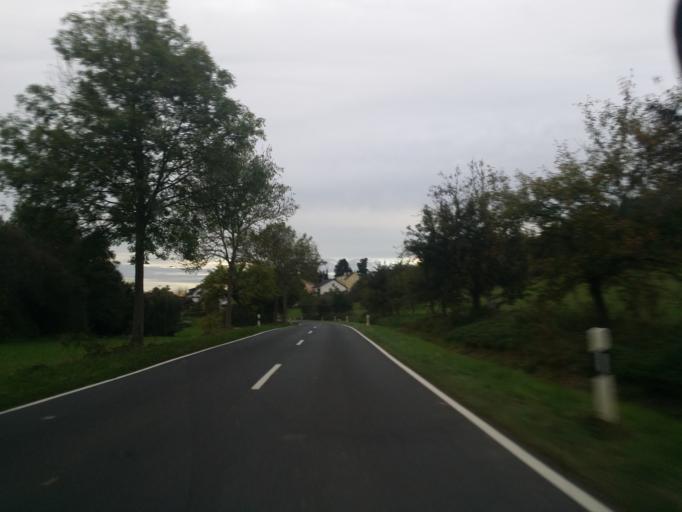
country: DE
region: Hesse
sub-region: Regierungsbezirk Darmstadt
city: Waldems
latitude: 50.2447
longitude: 8.3231
